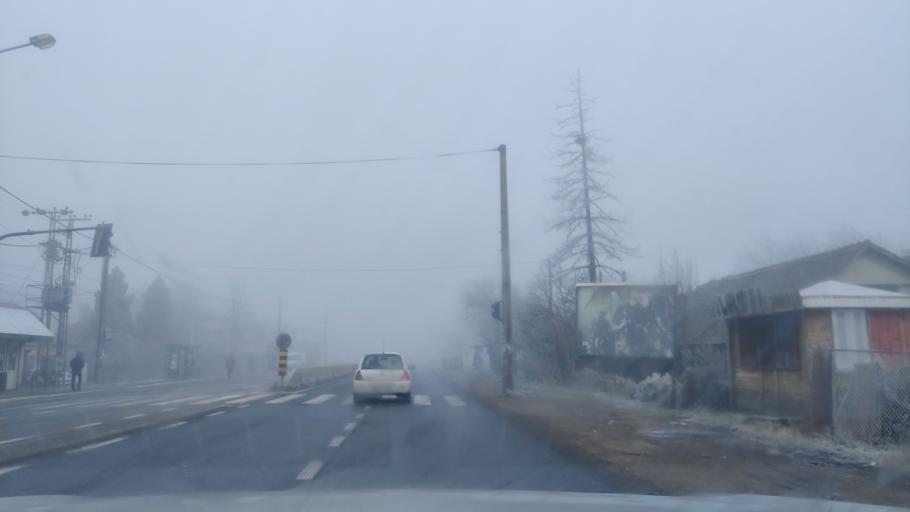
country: RS
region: Central Serbia
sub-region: Belgrade
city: Stari Grad
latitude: 44.8677
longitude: 20.4741
